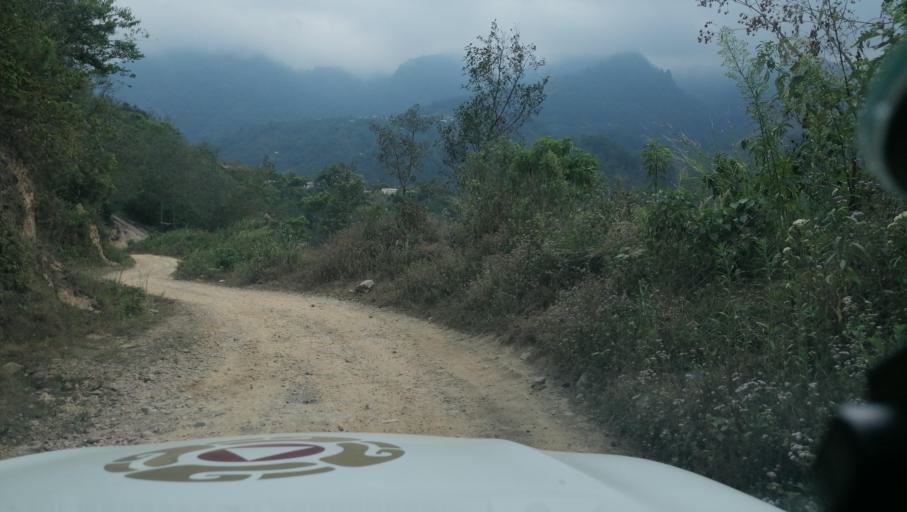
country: GT
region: San Marcos
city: Tacana
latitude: 15.2184
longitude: -92.1990
